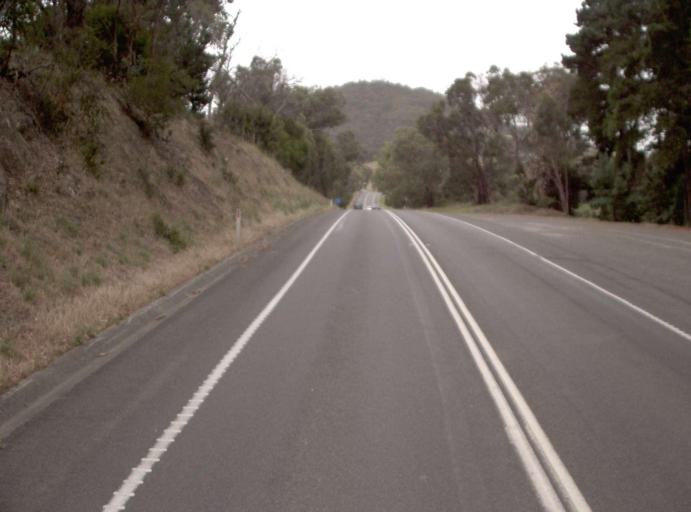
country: AU
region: Victoria
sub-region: Yarra Ranges
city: Yarra Glen
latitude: -37.5878
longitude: 145.4122
